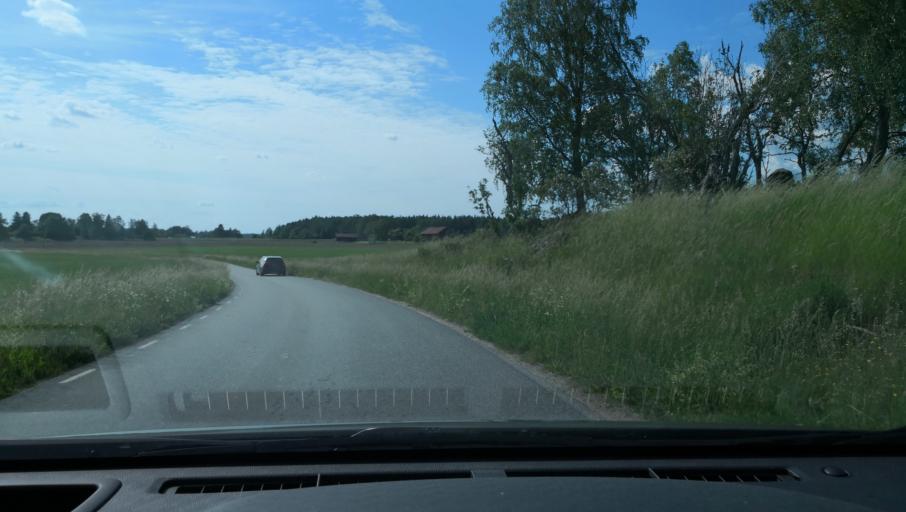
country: SE
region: Uppsala
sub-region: Enkopings Kommun
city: Orsundsbro
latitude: 59.8164
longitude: 17.3531
